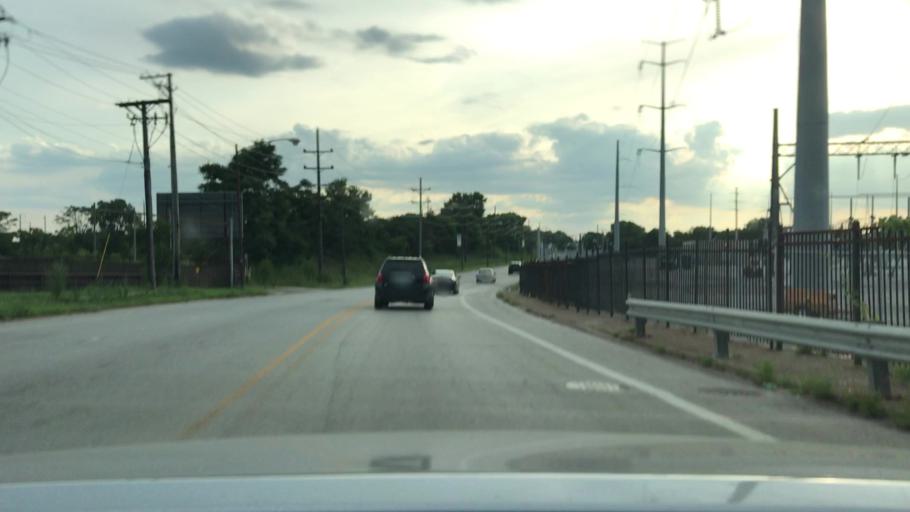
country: US
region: Indiana
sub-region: Lake County
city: Whiting
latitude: 41.7137
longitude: -87.5443
